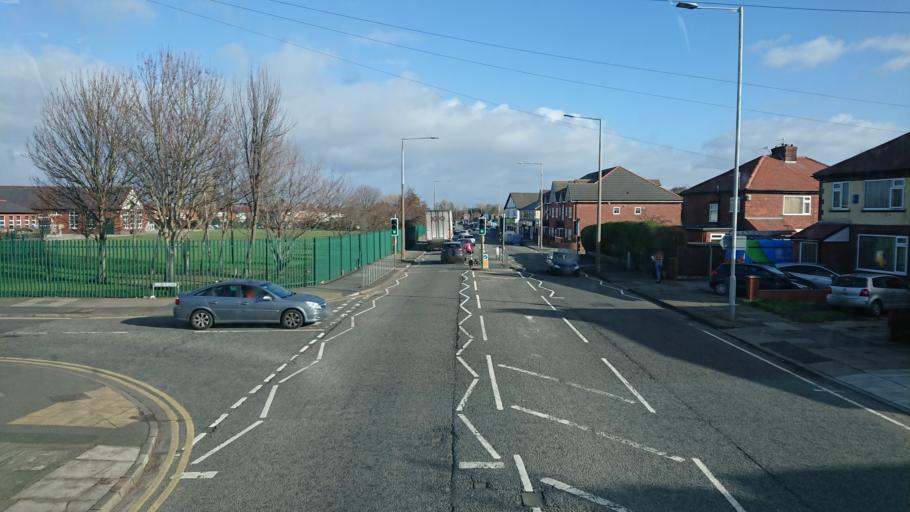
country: GB
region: England
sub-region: Metropolitan Borough of Wirral
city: Moreton
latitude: 53.4032
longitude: -3.1029
